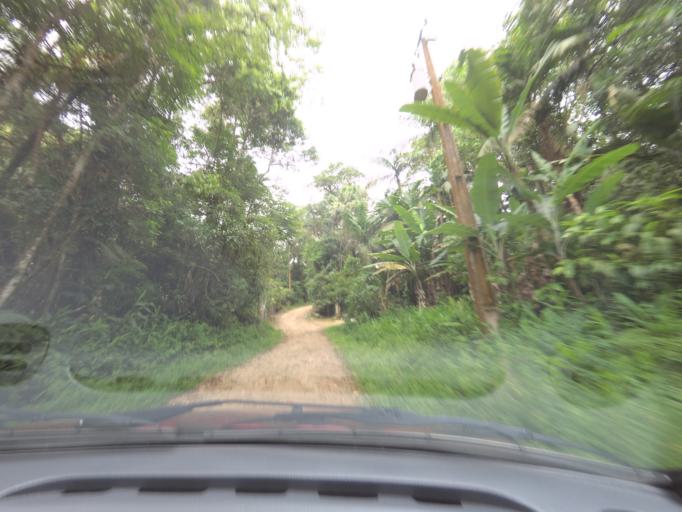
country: BR
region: Santa Catarina
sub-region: Brusque
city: Brusque
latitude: -27.0489
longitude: -48.9988
